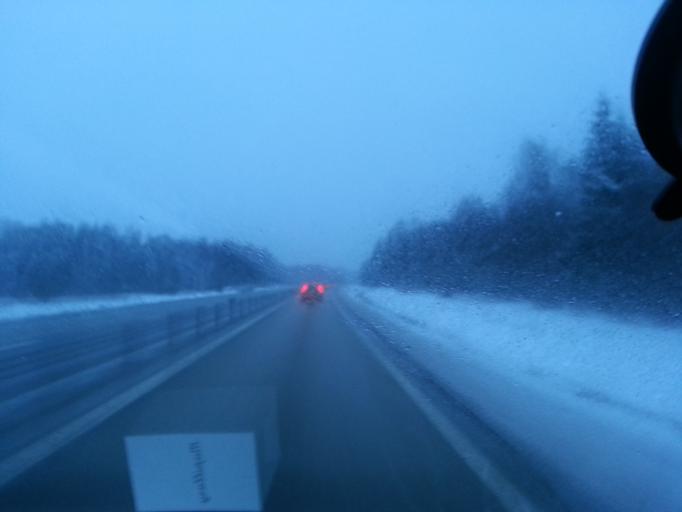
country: SE
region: Kronoberg
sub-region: Ljungby Kommun
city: Lagan
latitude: 57.0144
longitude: 14.0394
